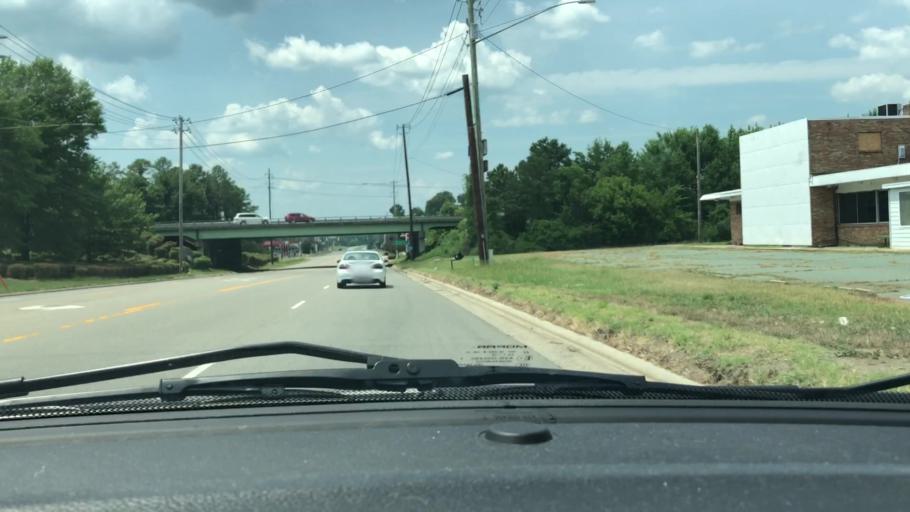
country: US
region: North Carolina
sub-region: Lee County
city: Sanford
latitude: 35.4944
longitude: -79.1940
